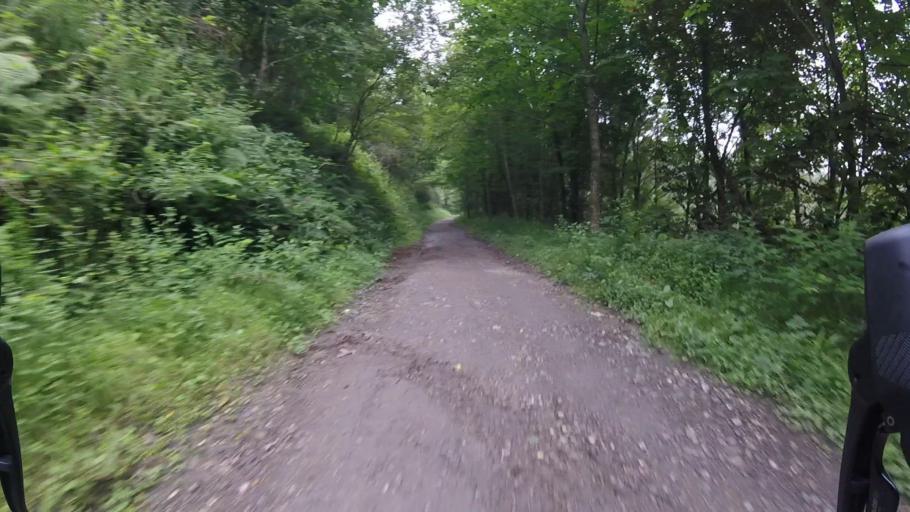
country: ES
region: Navarre
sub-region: Provincia de Navarra
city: Arano
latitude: 43.2564
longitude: -1.8877
